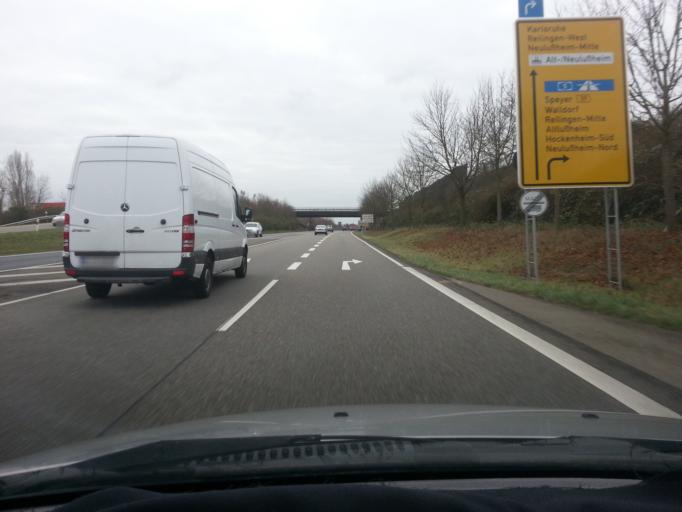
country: DE
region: Baden-Wuerttemberg
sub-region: Karlsruhe Region
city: Neulussheim
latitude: 49.3093
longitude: 8.5338
